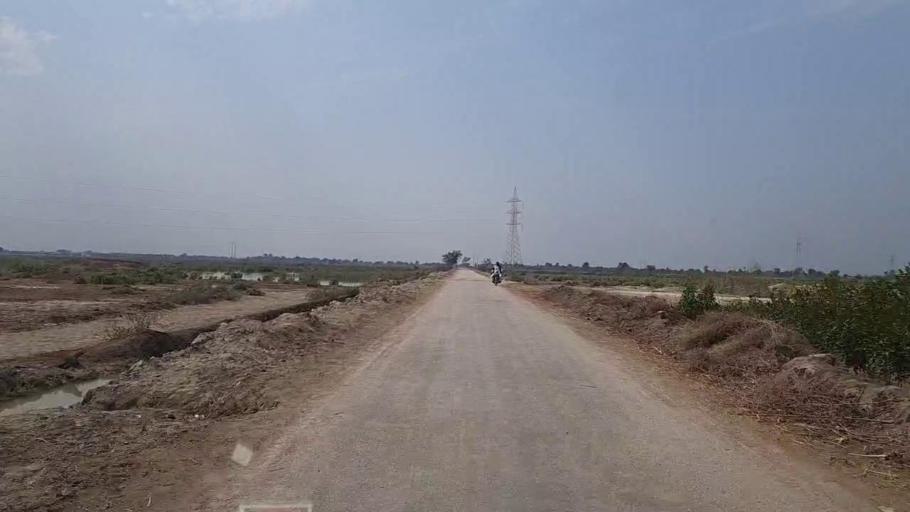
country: PK
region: Sindh
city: Mirwah Gorchani
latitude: 25.3371
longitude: 69.0464
